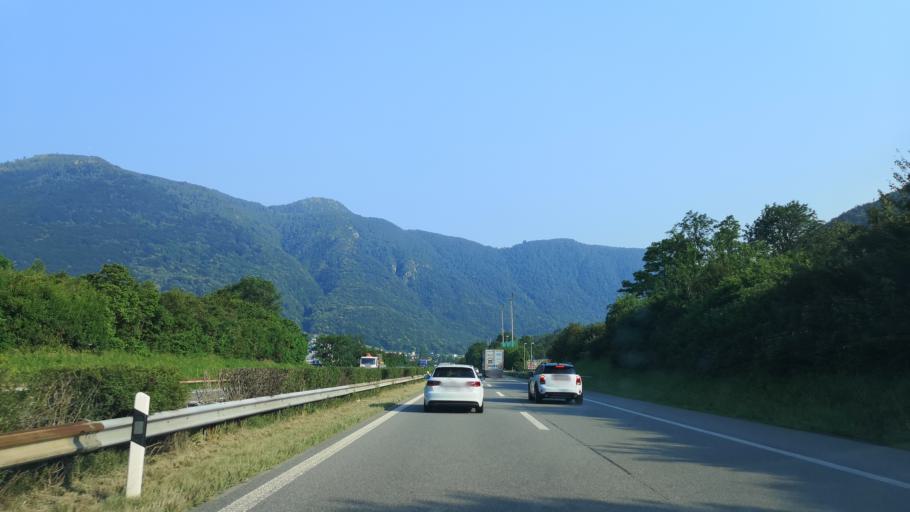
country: CH
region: Ticino
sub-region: Bellinzona District
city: Cadenazzo
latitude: 46.1169
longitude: 8.9266
